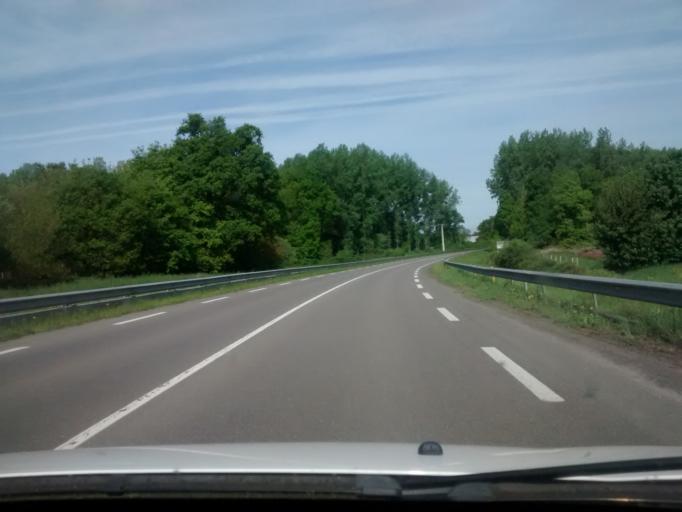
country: FR
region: Brittany
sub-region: Departement d'Ille-et-Vilaine
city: Saint-Brice-en-Cogles
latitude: 48.3961
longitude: -1.3678
